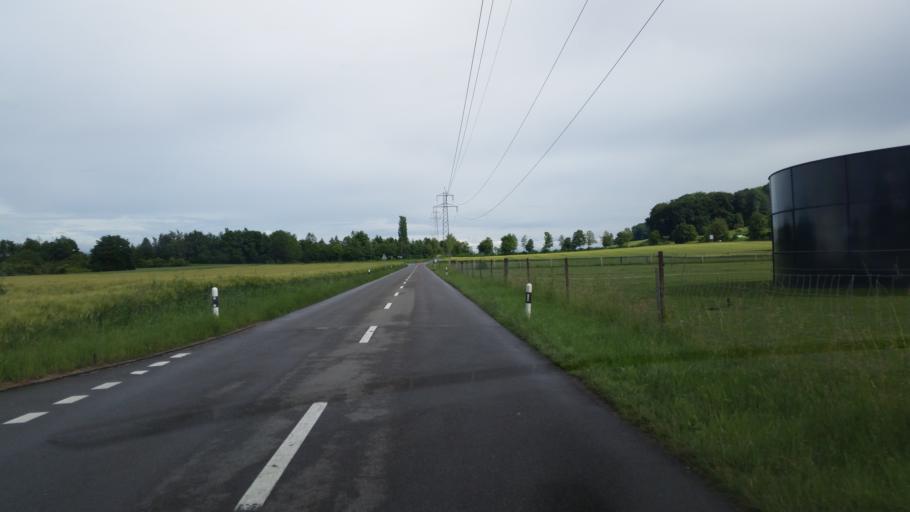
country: CH
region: Aargau
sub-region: Bezirk Muri
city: Waltenschwil
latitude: 47.3305
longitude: 8.2884
